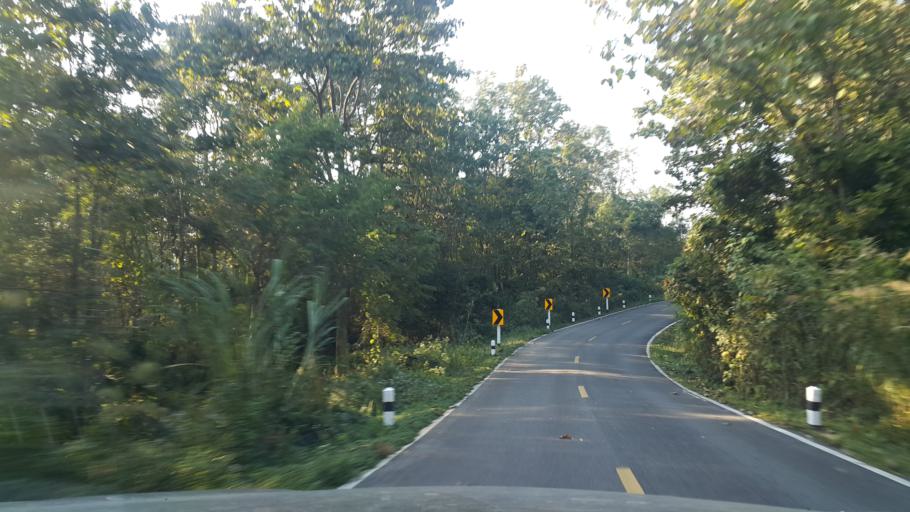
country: TH
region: Lampang
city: Hang Chat
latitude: 18.3516
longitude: 99.2490
